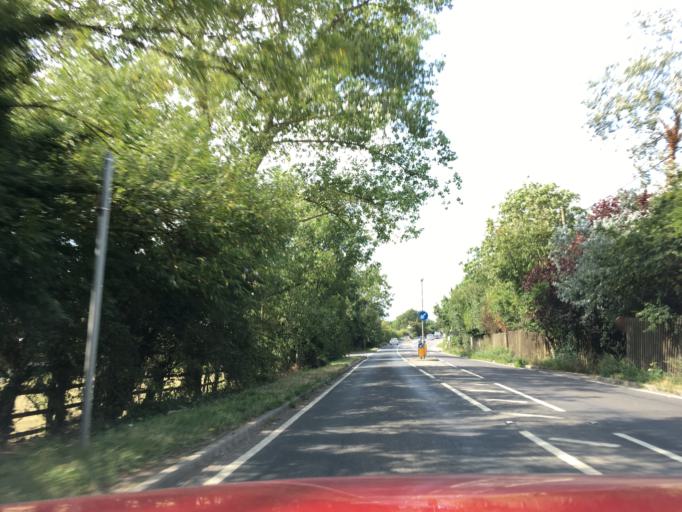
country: GB
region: England
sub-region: Kent
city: Headcorn
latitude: 51.1978
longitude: 0.5968
